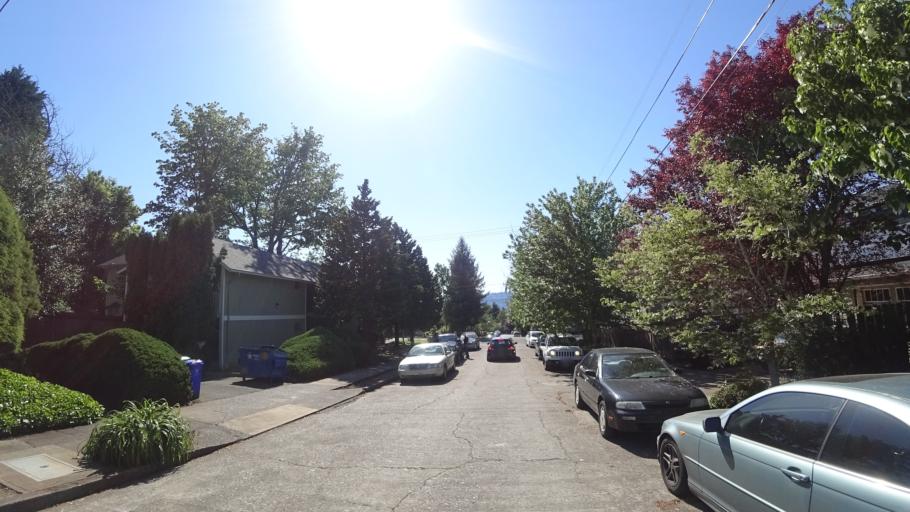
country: US
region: Oregon
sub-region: Clackamas County
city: Milwaukie
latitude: 45.4896
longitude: -122.6191
